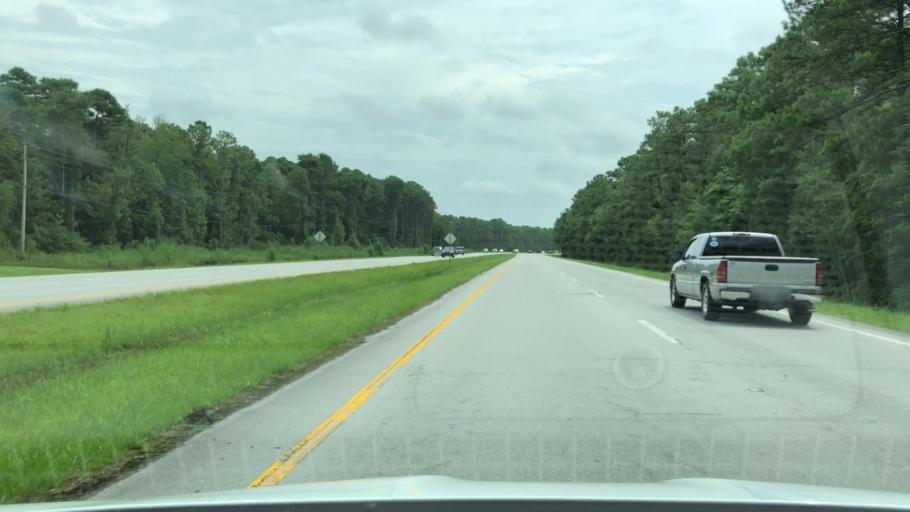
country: US
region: North Carolina
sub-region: Craven County
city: Havelock
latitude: 34.8533
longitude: -76.8918
